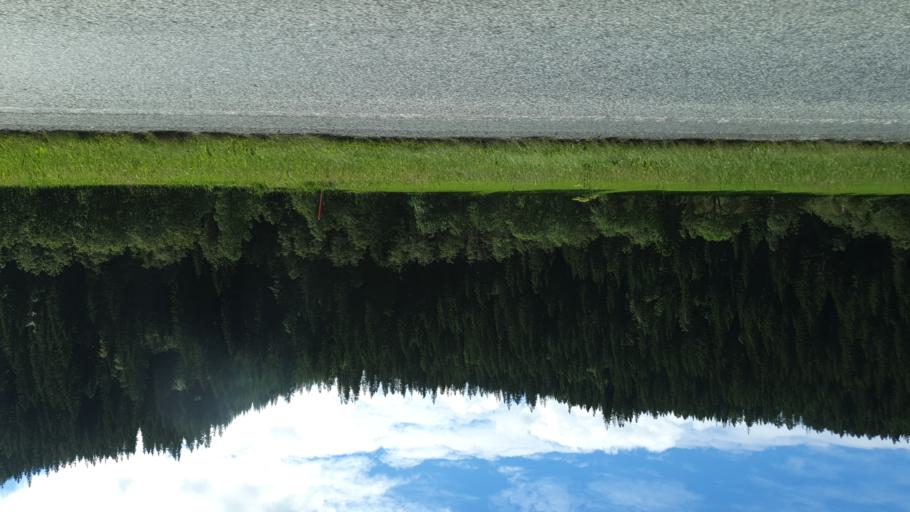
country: NO
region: Sor-Trondelag
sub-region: Midtre Gauldal
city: Storen
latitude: 63.0129
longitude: 10.2466
